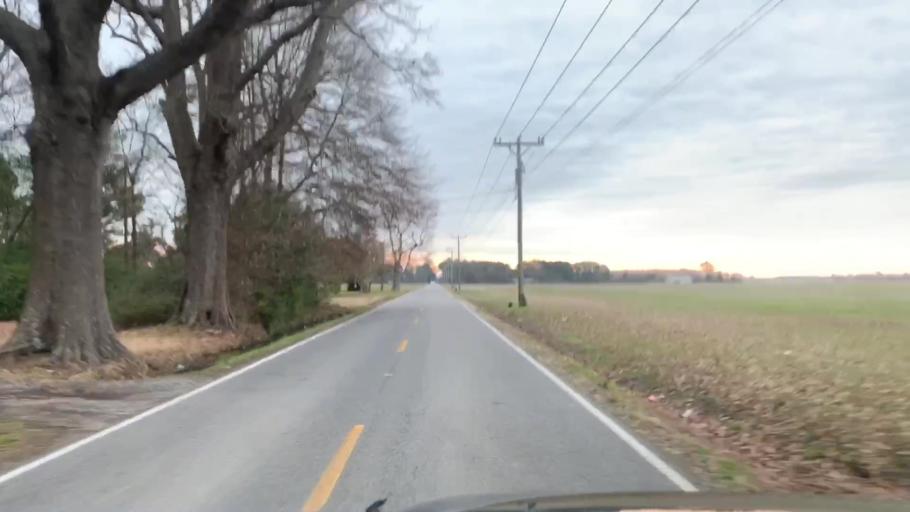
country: US
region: North Carolina
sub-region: Currituck County
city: Moyock
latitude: 36.6345
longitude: -76.1877
